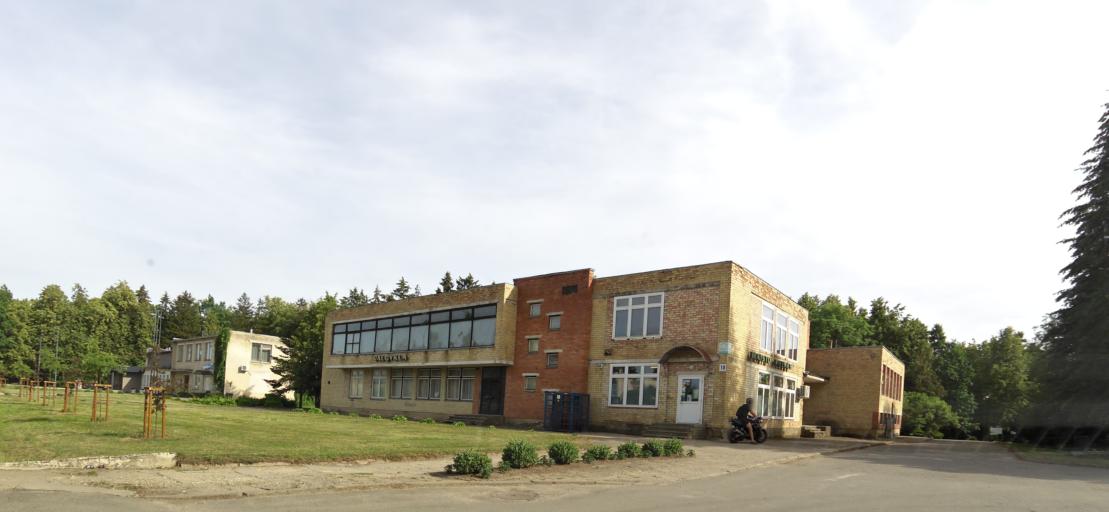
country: LT
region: Panevezys
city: Pasvalys
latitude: 56.1083
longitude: 24.4922
